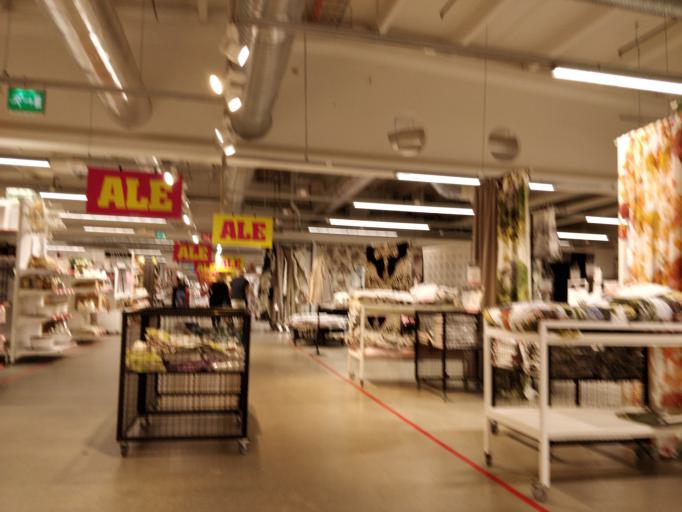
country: FI
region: Paijanne Tavastia
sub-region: Lahti
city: Lahti
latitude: 60.9338
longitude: 25.6247
